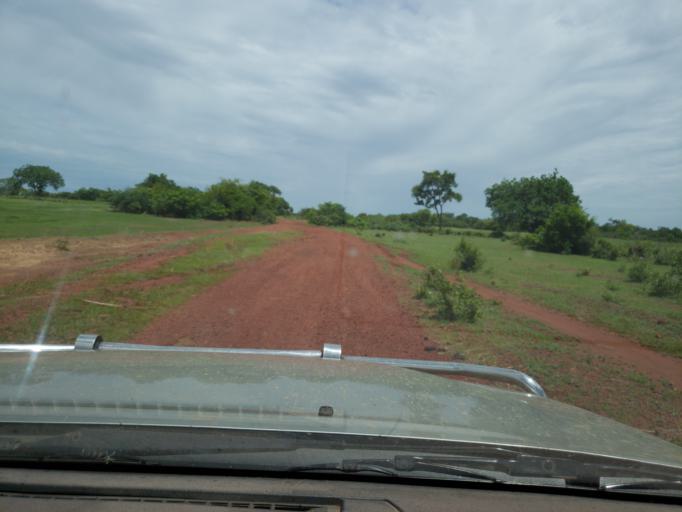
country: ML
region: Sikasso
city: Sikasso
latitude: 11.6784
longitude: -6.1845
